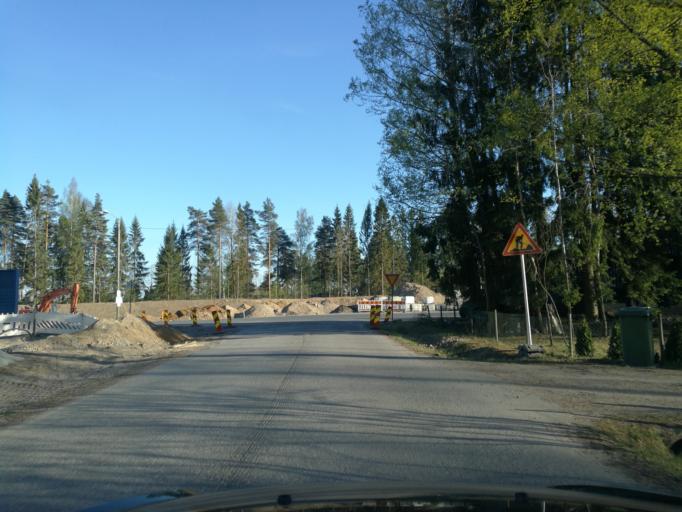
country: FI
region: Uusimaa
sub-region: Helsinki
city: Tuusula
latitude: 60.4052
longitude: 24.9959
